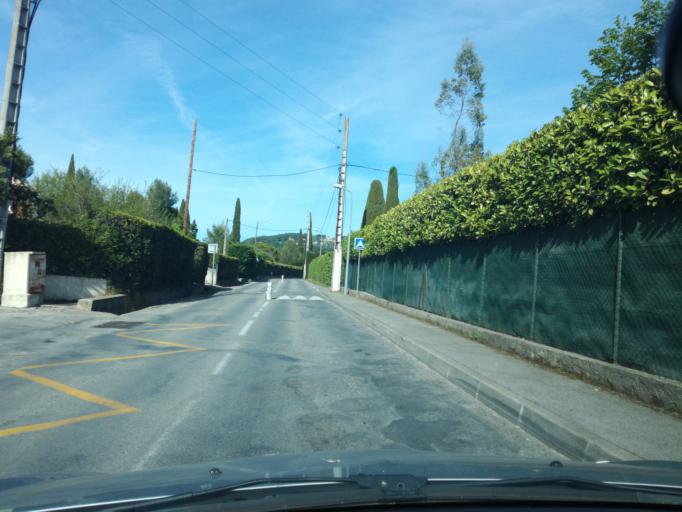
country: FR
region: Provence-Alpes-Cote d'Azur
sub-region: Departement des Alpes-Maritimes
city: Mouans-Sartoux
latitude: 43.6232
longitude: 6.9569
